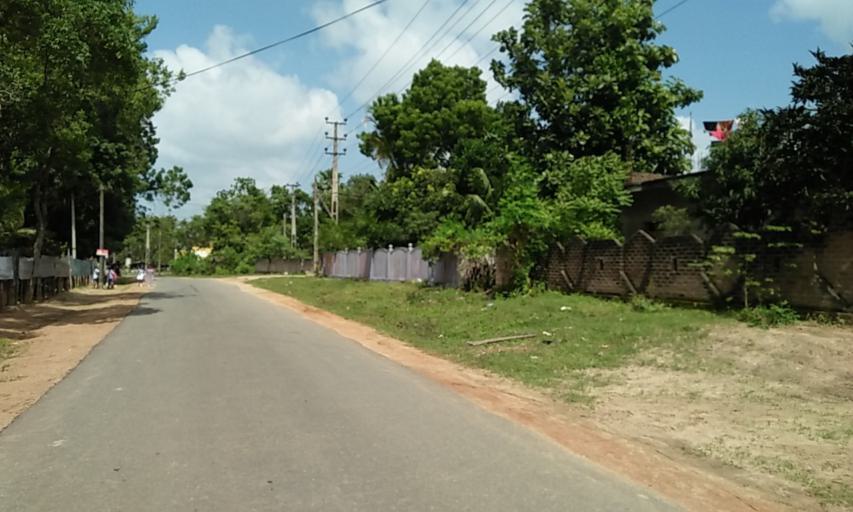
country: LK
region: Eastern Province
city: Ampara
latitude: 7.3356
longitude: 81.7430
